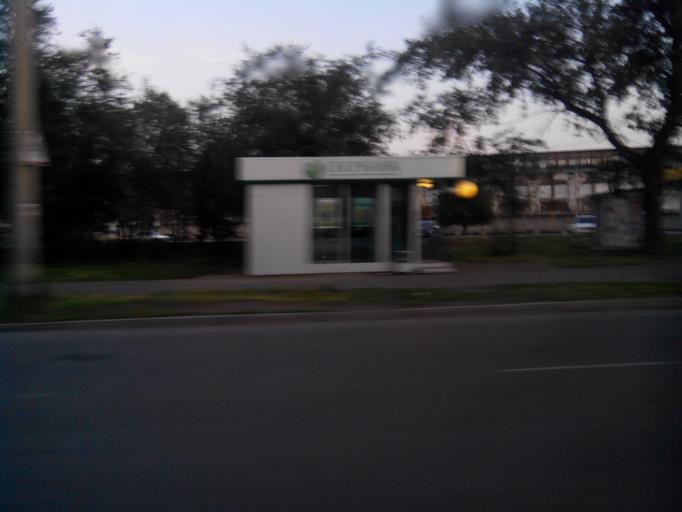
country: RU
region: Krasnoyarskiy
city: Krasnoyarsk
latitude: 56.0068
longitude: 92.8345
